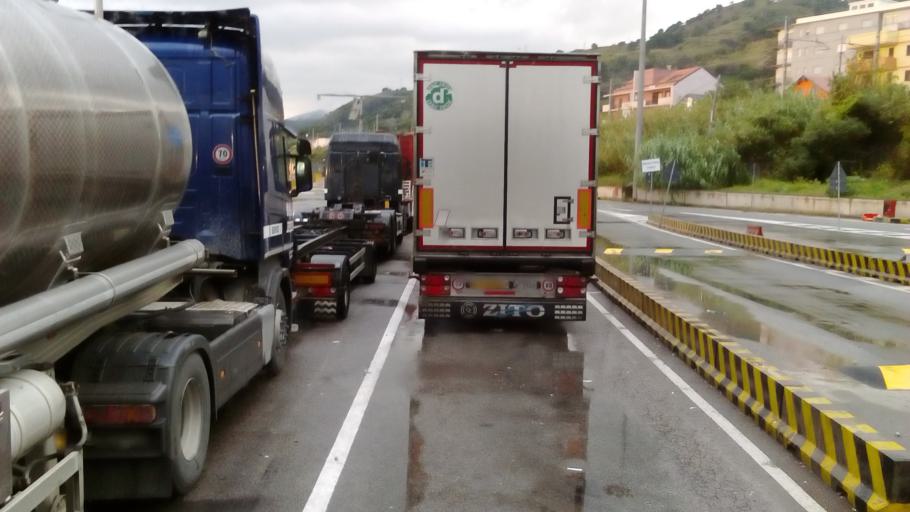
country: IT
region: Sicily
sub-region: Messina
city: Larderia
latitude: 38.1328
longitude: 15.5241
